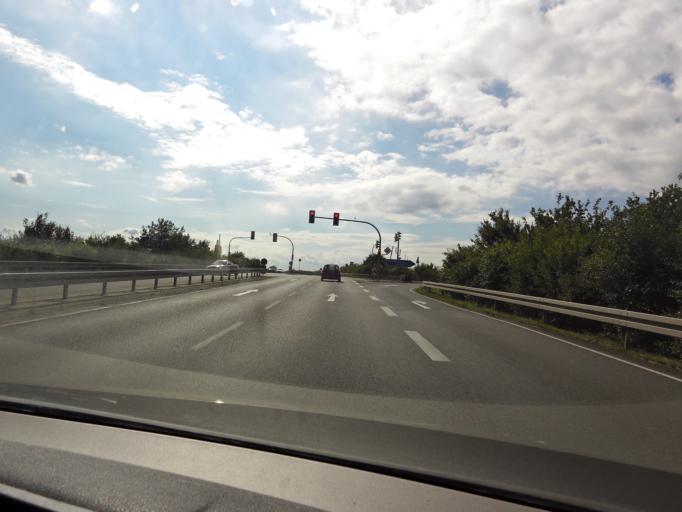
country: DE
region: Saxony
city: Taucha
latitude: 51.3559
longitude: 12.4968
